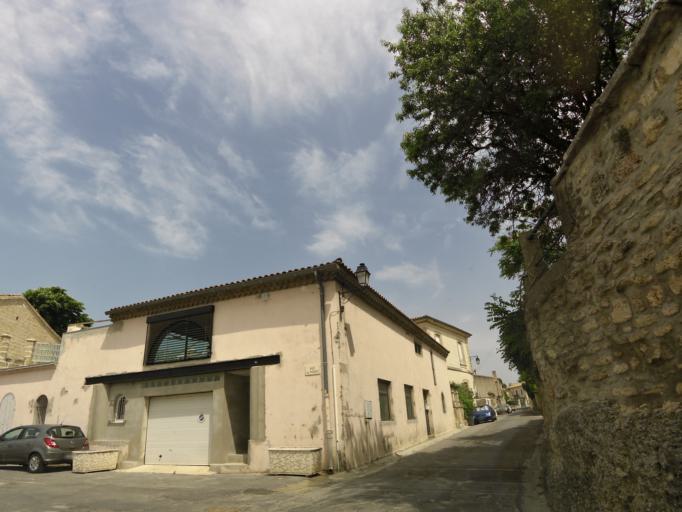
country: FR
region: Languedoc-Roussillon
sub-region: Departement du Gard
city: Aubais
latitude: 43.7690
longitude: 4.1225
